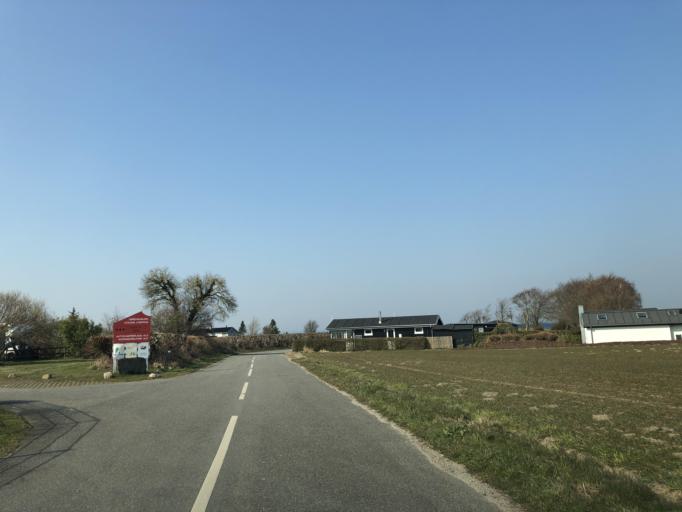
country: DK
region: South Denmark
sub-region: Sonderborg Kommune
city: Nordborg
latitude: 55.0787
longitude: 9.7294
